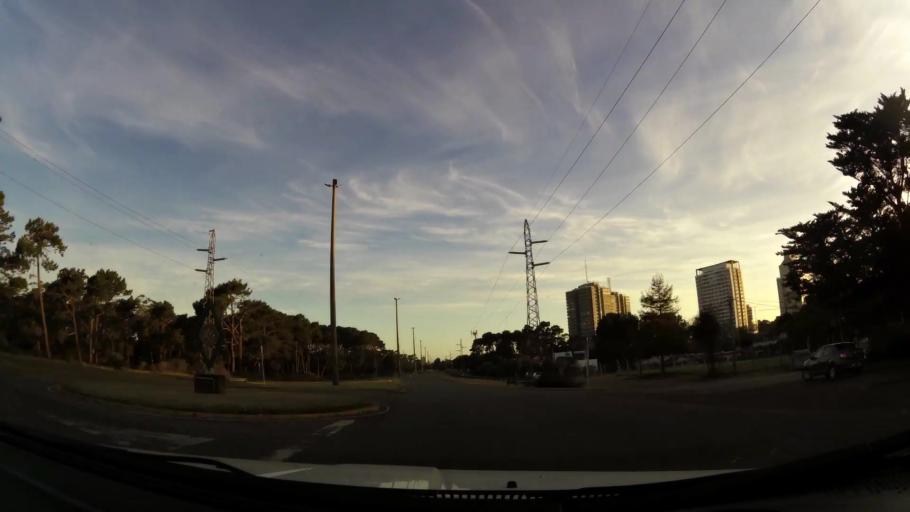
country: UY
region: Maldonado
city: Maldonado
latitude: -34.9287
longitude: -54.9403
